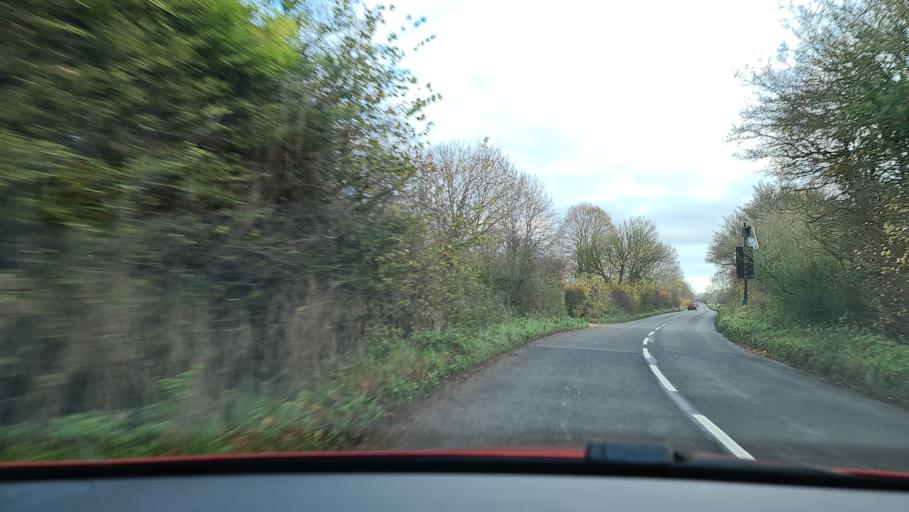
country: GB
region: England
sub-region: Buckinghamshire
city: Princes Risborough
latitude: 51.7219
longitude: -0.8720
